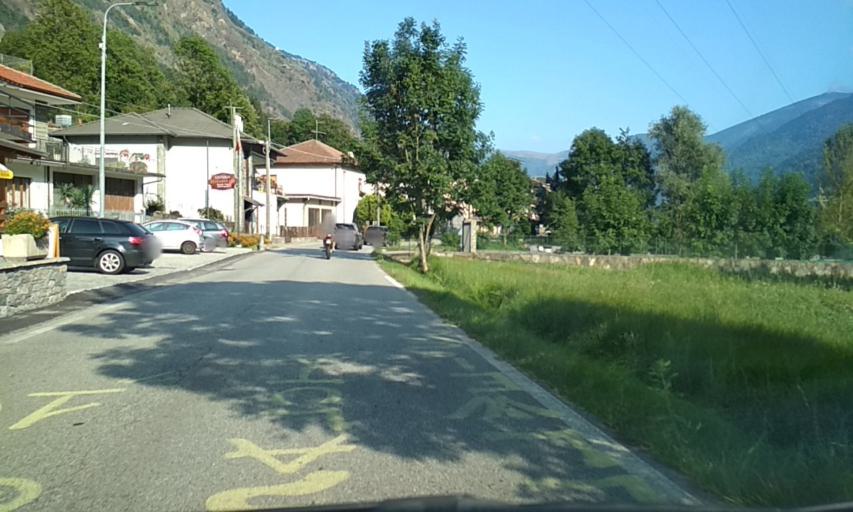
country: IT
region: Piedmont
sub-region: Provincia di Torino
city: Locana
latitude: 45.4189
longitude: 7.4505
